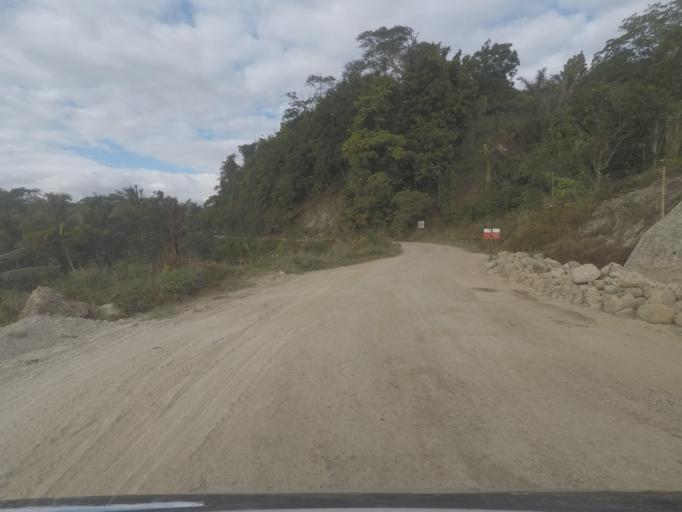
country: TL
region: Baucau
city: Venilale
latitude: -8.6077
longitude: 126.3825
